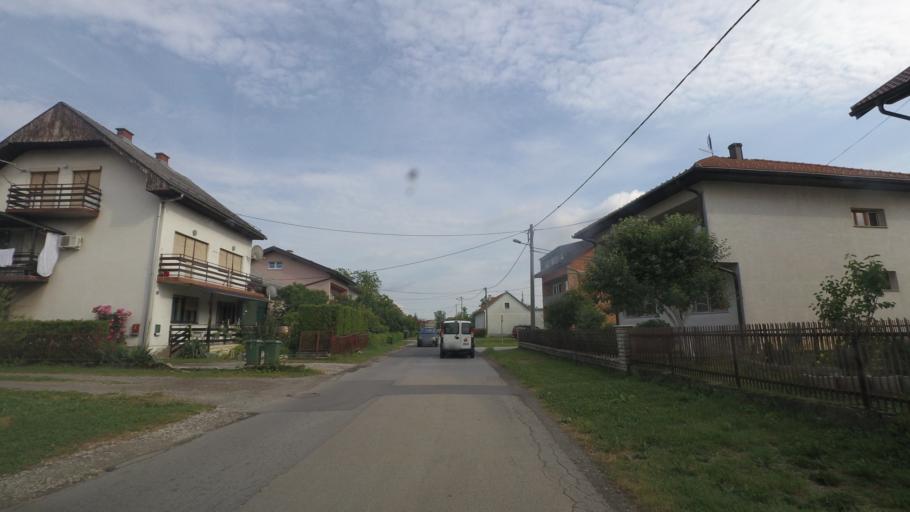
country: HR
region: Karlovacka
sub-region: Grad Karlovac
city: Karlovac
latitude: 45.5031
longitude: 15.5327
